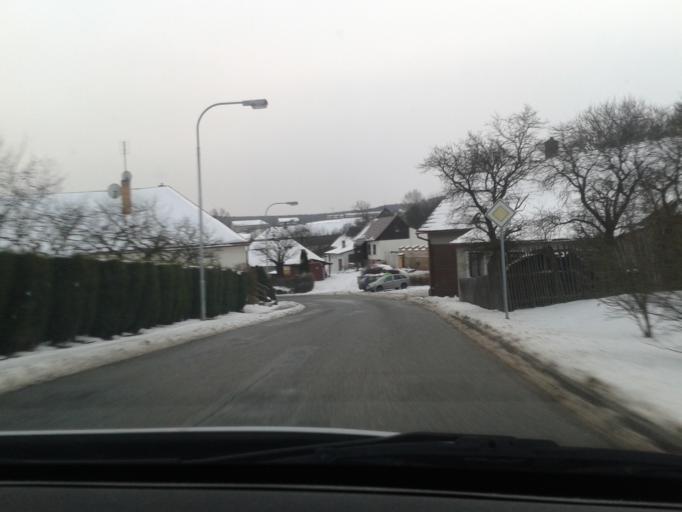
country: CZ
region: Olomoucky
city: Protivanov
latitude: 49.5276
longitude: 16.8614
